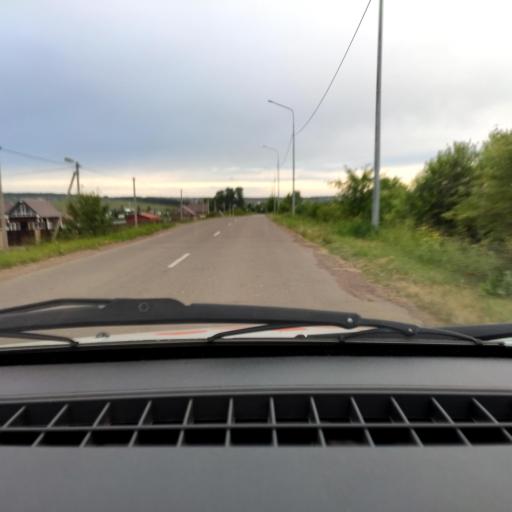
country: RU
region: Bashkortostan
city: Avdon
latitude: 54.5412
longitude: 55.7612
